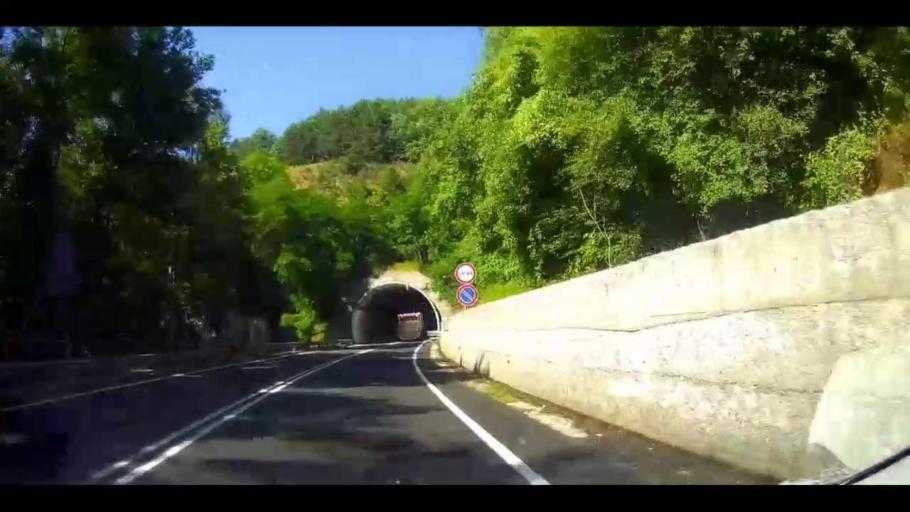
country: IT
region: Calabria
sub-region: Provincia di Cosenza
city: Celico
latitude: 39.3349
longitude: 16.3593
